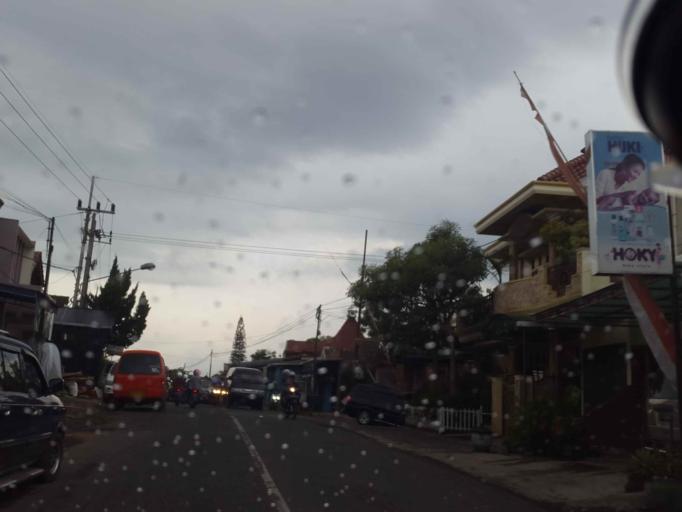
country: ID
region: East Java
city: Batu
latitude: -7.8437
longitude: 112.5282
